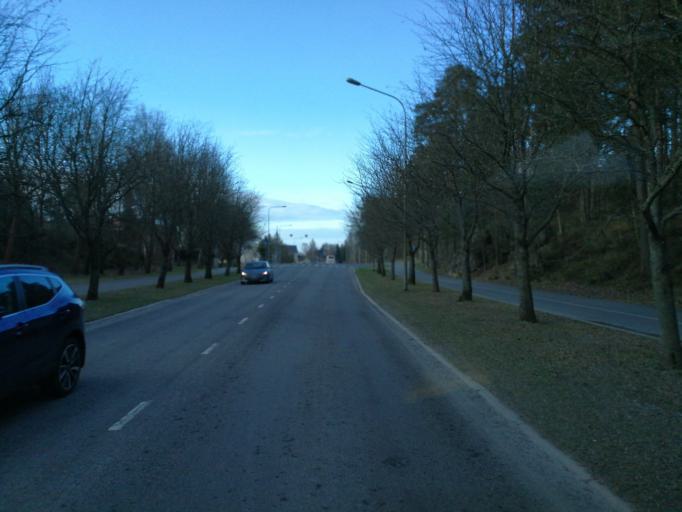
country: FI
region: Varsinais-Suomi
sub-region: Turku
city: Turku
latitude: 60.4293
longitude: 22.2916
